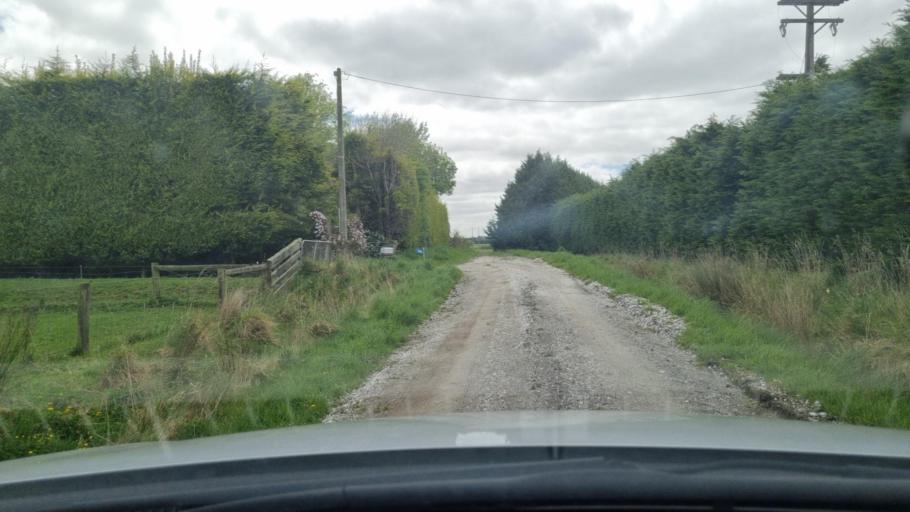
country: NZ
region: Southland
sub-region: Invercargill City
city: Invercargill
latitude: -46.3894
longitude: 168.4043
